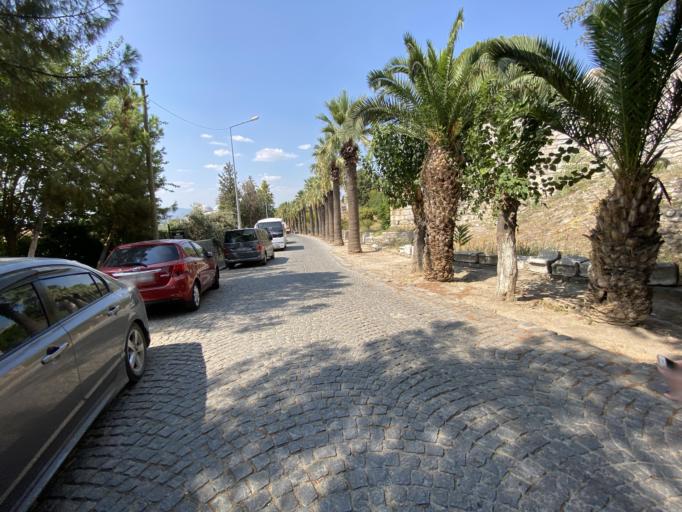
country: TR
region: Izmir
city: Selcuk
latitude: 37.9513
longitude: 27.3678
